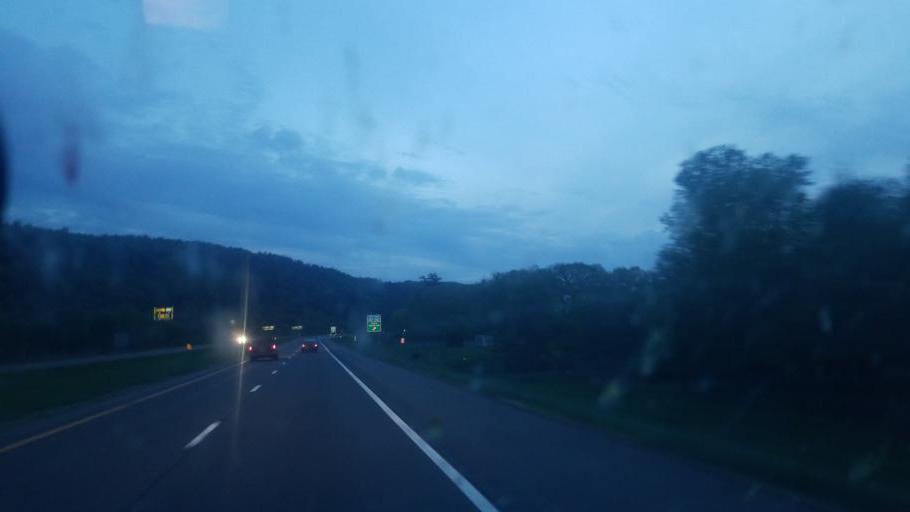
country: US
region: New York
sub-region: Tioga County
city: Owego
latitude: 42.0900
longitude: -76.2727
